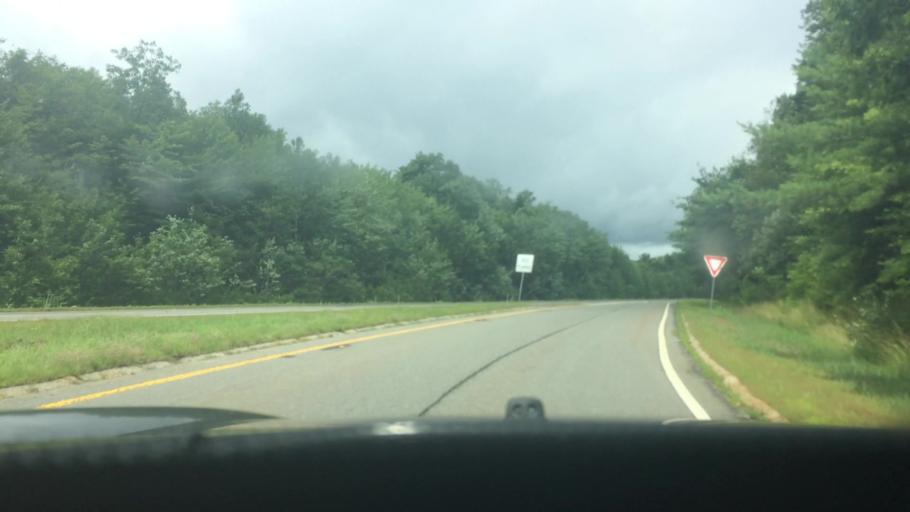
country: US
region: Massachusetts
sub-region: Worcester County
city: Templeton
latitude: 42.5602
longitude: -72.0499
